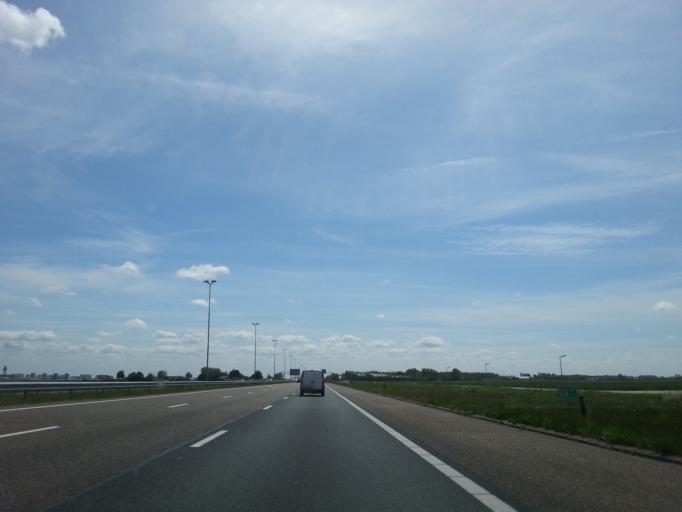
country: NL
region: North Holland
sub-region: Gemeente Haarlemmermeer
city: Hoofddorp
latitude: 52.3442
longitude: 4.7352
